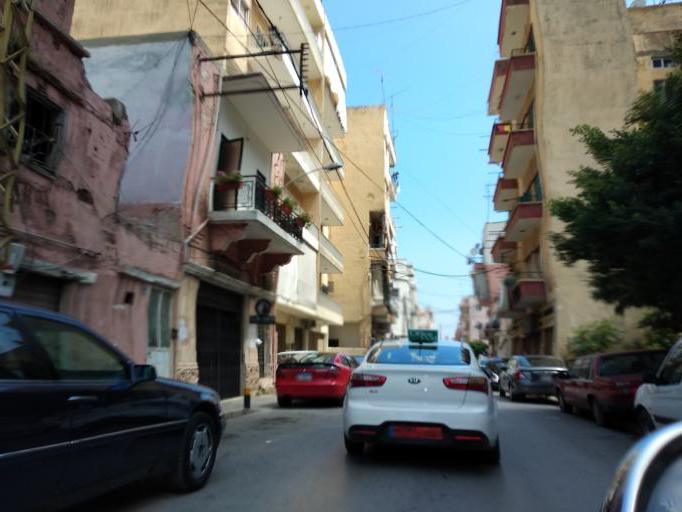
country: LB
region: Mont-Liban
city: Jdaidet el Matn
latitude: 33.8934
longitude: 35.5336
